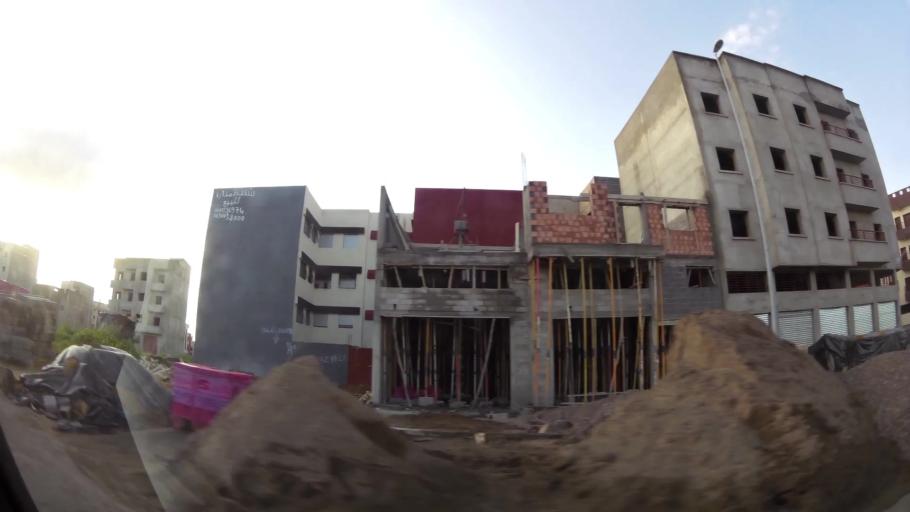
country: MA
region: Chaouia-Ouardigha
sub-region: Settat Province
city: Settat
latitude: 32.9946
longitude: -7.6340
